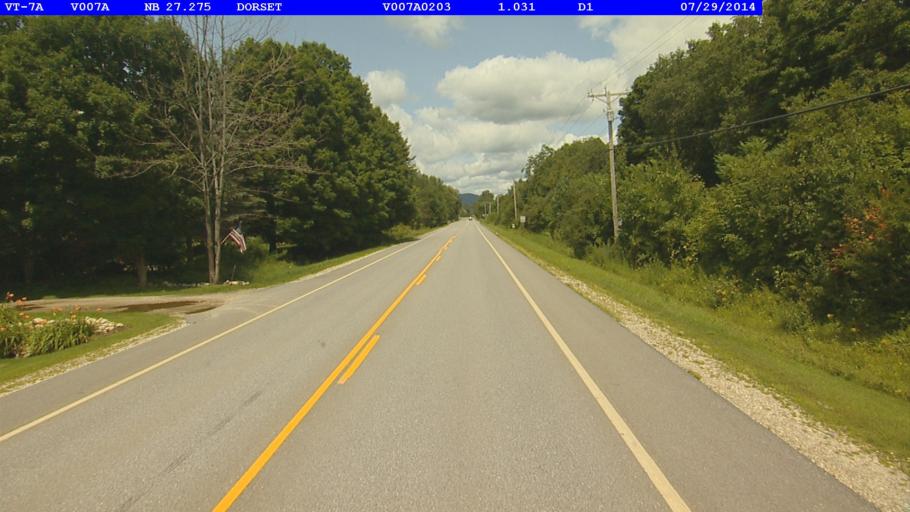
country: US
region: Vermont
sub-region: Bennington County
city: Manchester Center
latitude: 43.2244
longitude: -73.0115
